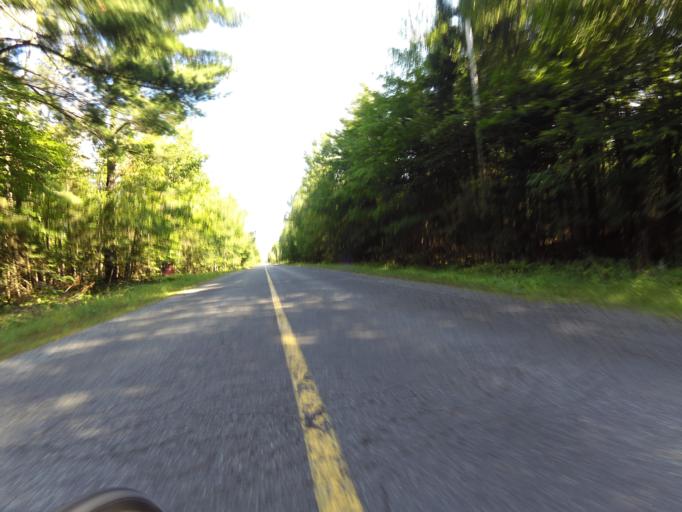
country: CA
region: Ontario
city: Bells Corners
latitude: 45.4753
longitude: -76.0188
